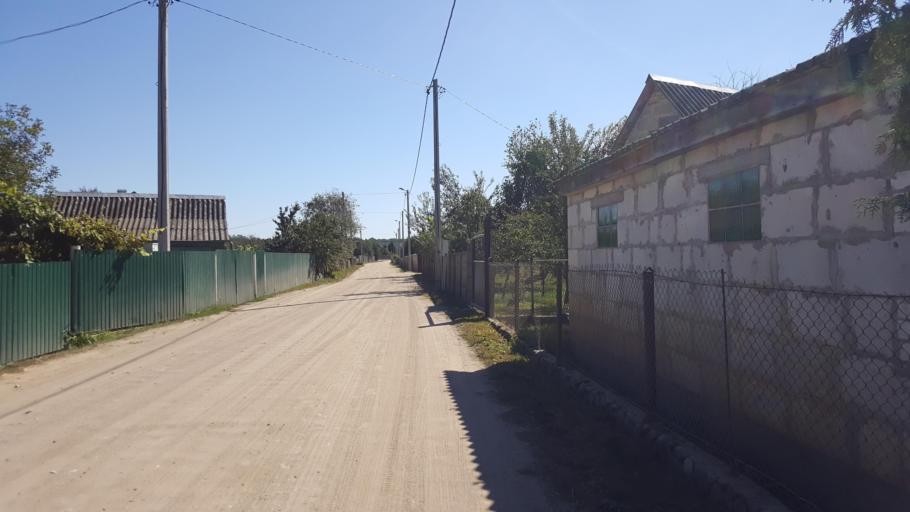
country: BY
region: Brest
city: Vysokaye
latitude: 52.2527
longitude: 23.4935
